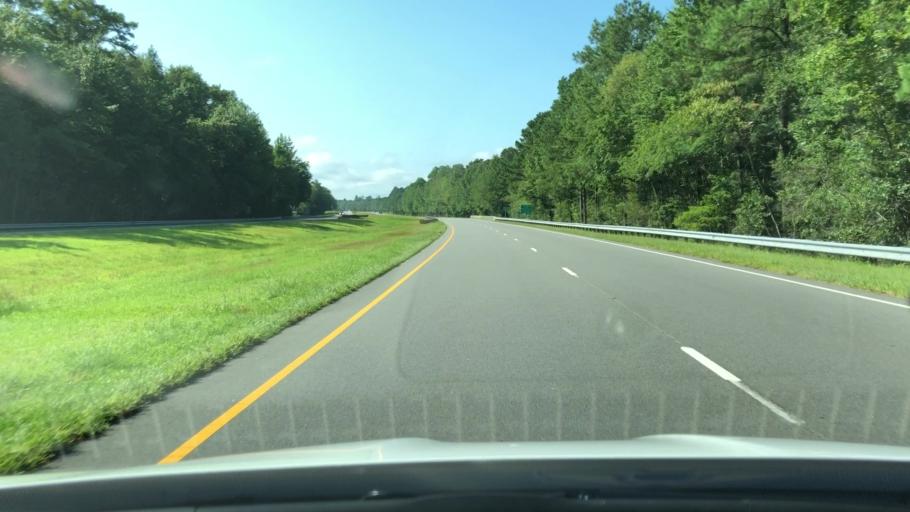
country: US
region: North Carolina
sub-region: Pasquotank County
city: Elizabeth City
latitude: 36.4234
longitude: -76.3427
